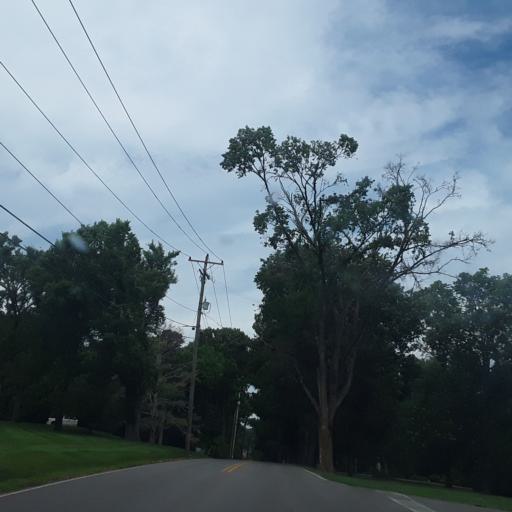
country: US
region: Tennessee
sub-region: Davidson County
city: Oak Hill
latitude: 36.0776
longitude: -86.7745
